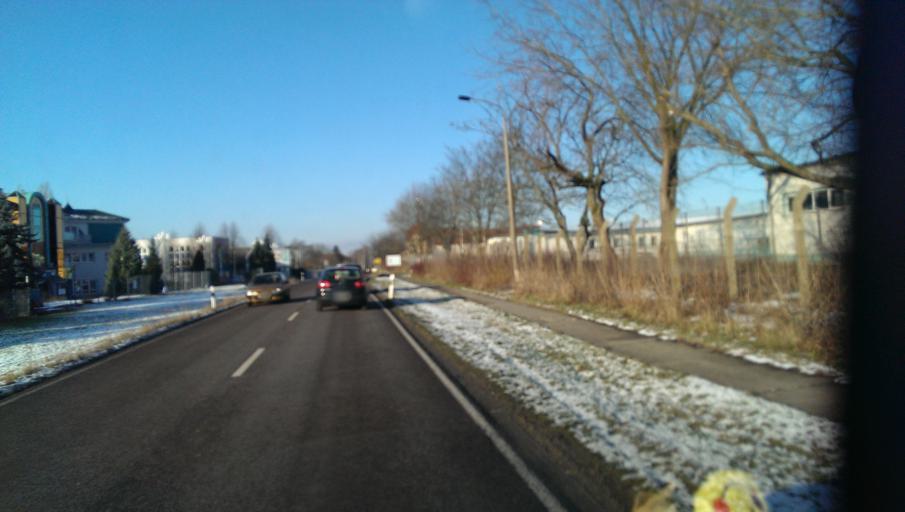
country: DE
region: Saxony
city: Wilsdruff
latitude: 51.0382
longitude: 13.5454
